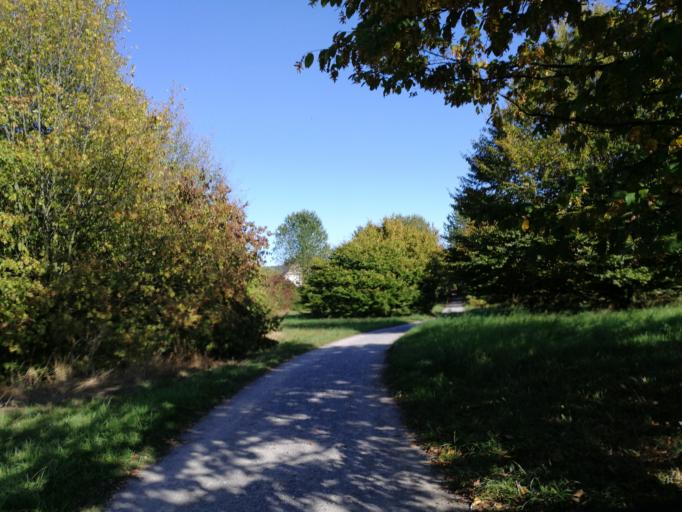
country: DE
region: North Rhine-Westphalia
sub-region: Regierungsbezirk Dusseldorf
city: Neuss
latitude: 51.1332
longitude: 6.7378
